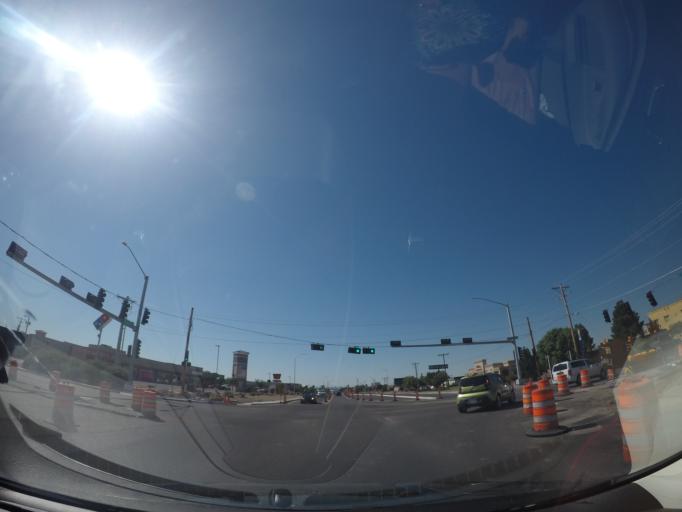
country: US
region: New Mexico
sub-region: Dona Ana County
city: Las Cruces
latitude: 32.2937
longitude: -106.7859
